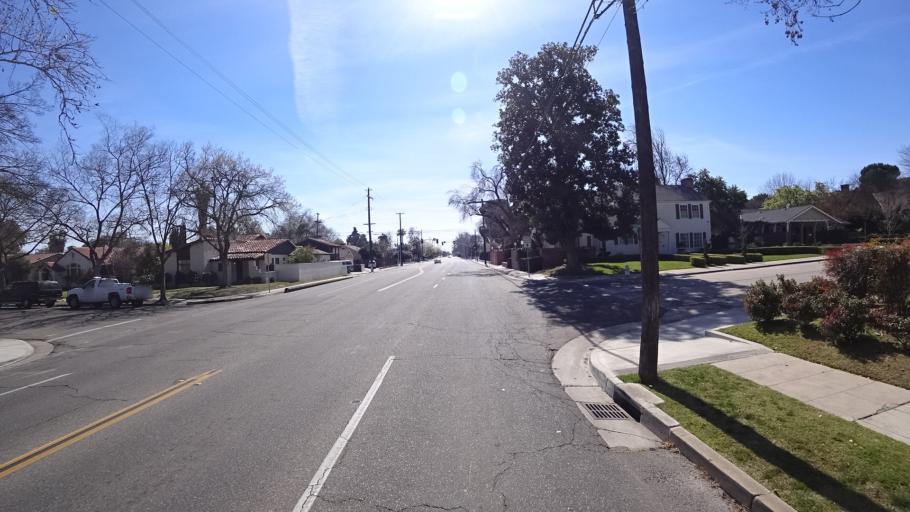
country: US
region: California
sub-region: Fresno County
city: Fresno
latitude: 36.7733
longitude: -119.8087
